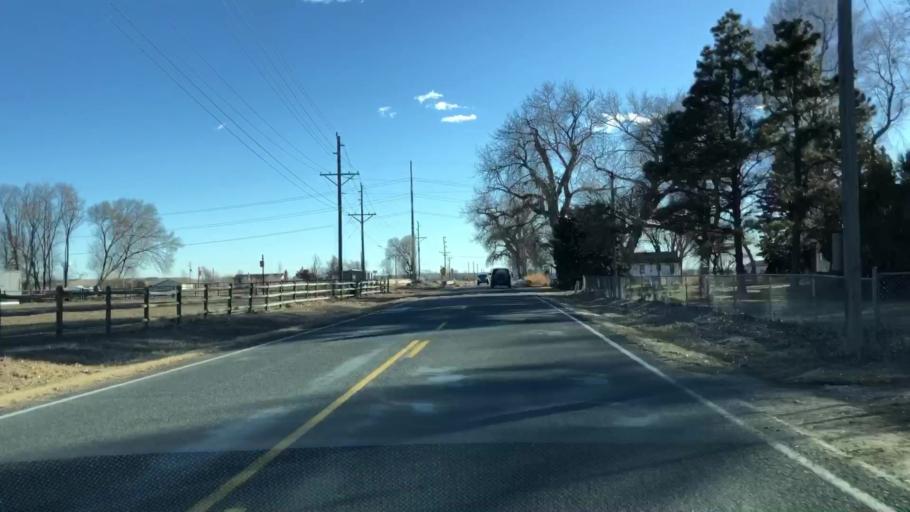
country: US
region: Colorado
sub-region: Larimer County
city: Fort Collins
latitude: 40.5618
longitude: -104.9822
